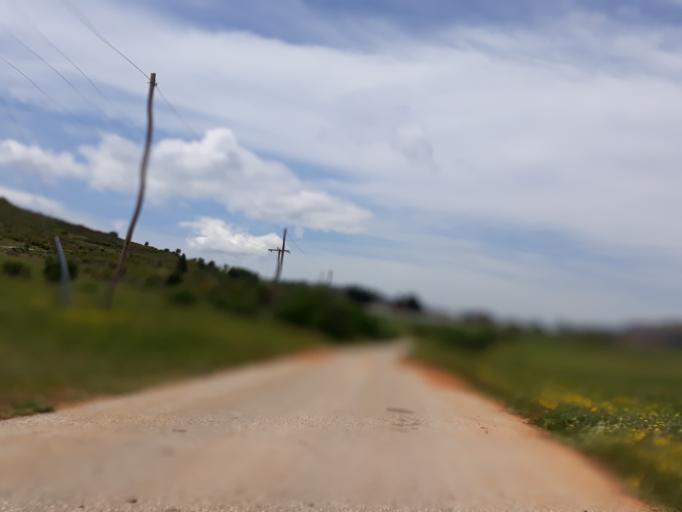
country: GR
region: Central Greece
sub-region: Nomos Voiotias
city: Ayios Thomas
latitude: 38.1812
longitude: 23.5556
